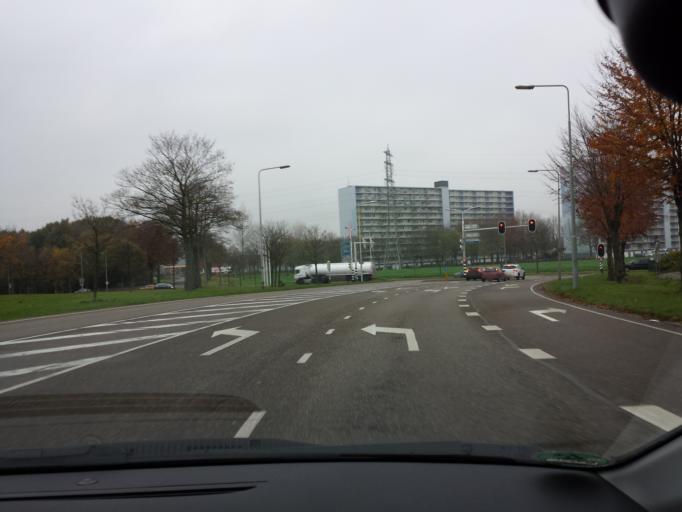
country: NL
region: Limburg
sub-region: Gemeente Heerlen
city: Heerlen
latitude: 50.8613
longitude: 6.0117
